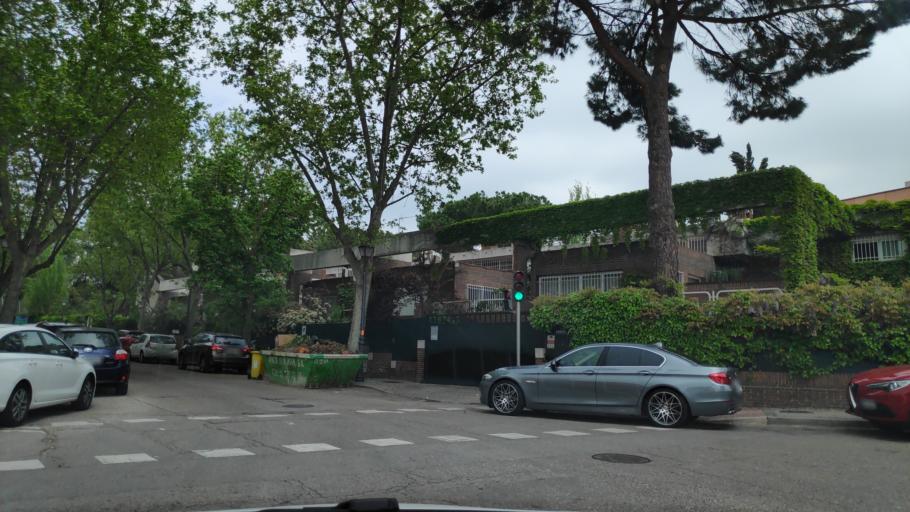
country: ES
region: Madrid
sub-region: Provincia de Madrid
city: Pozuelo de Alarcon
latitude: 40.4598
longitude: -3.7790
